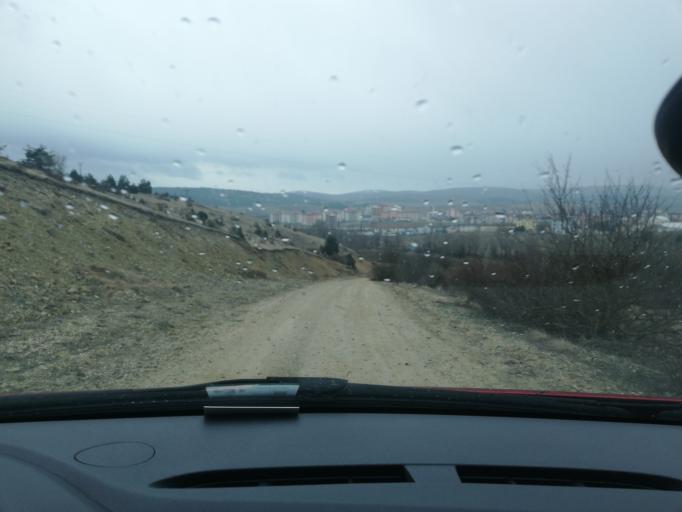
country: TR
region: Kastamonu
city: Seydiler
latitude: 41.6235
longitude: 33.7252
